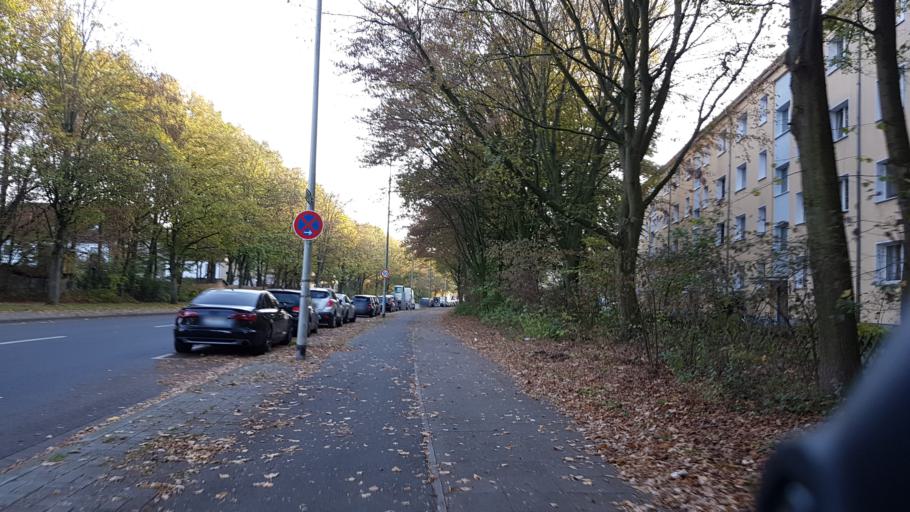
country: DE
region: Lower Saxony
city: Hemmingen
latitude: 52.3317
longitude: 9.7017
